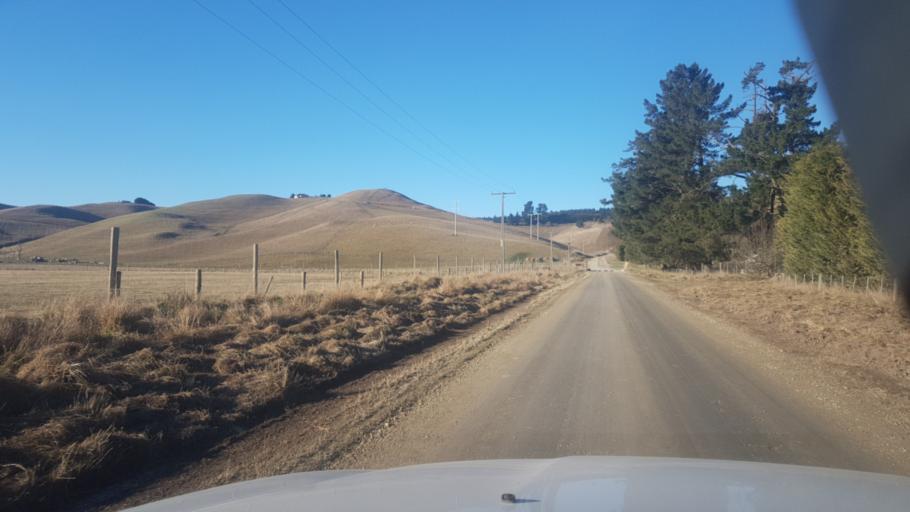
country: NZ
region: Canterbury
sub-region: Timaru District
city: Pleasant Point
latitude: -44.3434
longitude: 171.0580
